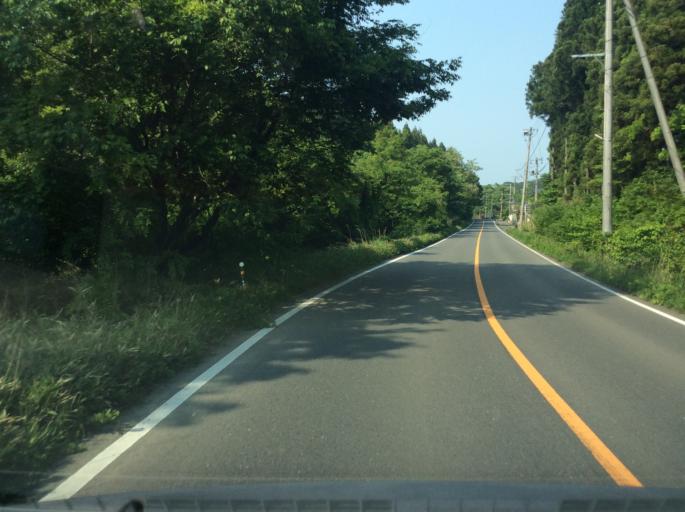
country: JP
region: Tochigi
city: Kuroiso
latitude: 37.0909
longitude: 140.2232
